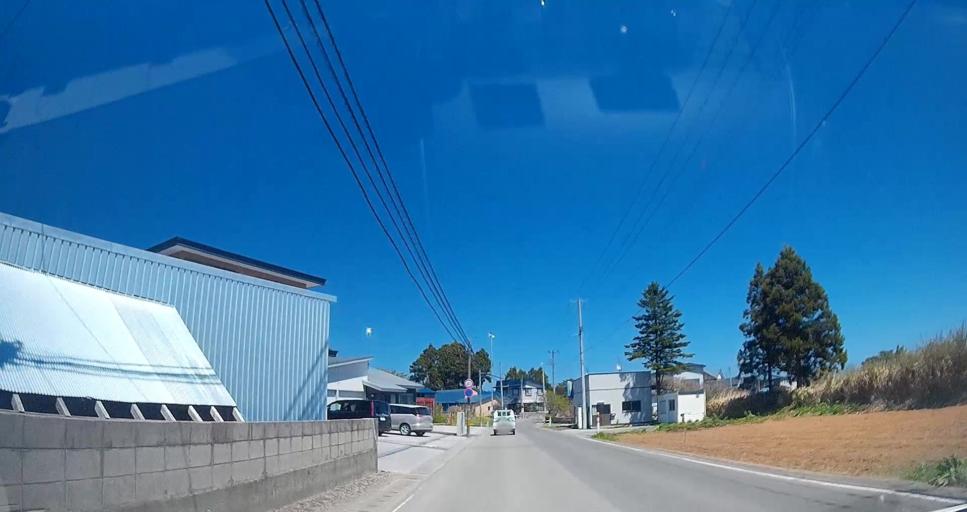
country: JP
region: Aomori
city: Mutsu
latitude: 41.2270
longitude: 141.3938
